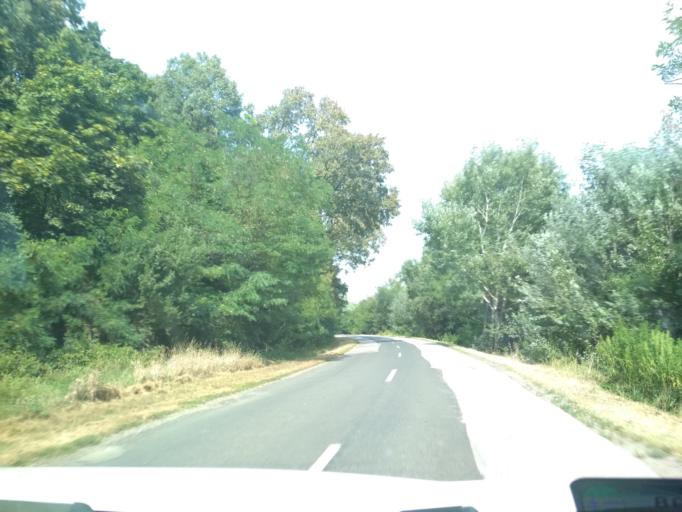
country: HU
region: Jasz-Nagykun-Szolnok
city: Tiszaszolos
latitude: 47.5205
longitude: 20.6653
